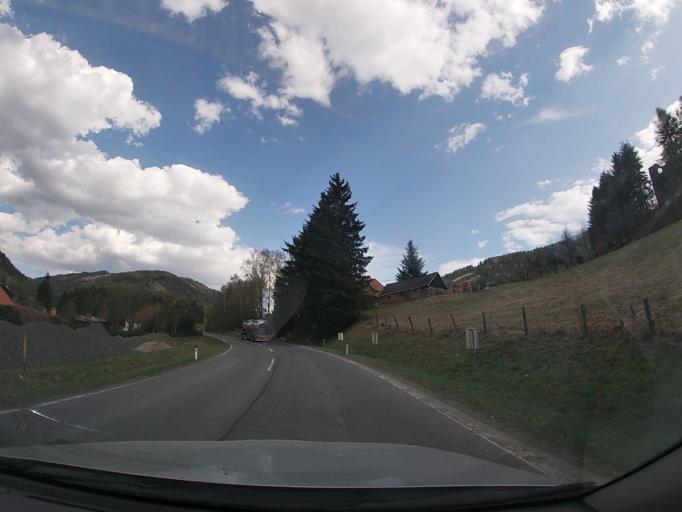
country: AT
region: Styria
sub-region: Politischer Bezirk Murau
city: Sankt Lorenzen bei Scheifling
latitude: 47.1428
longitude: 14.4180
